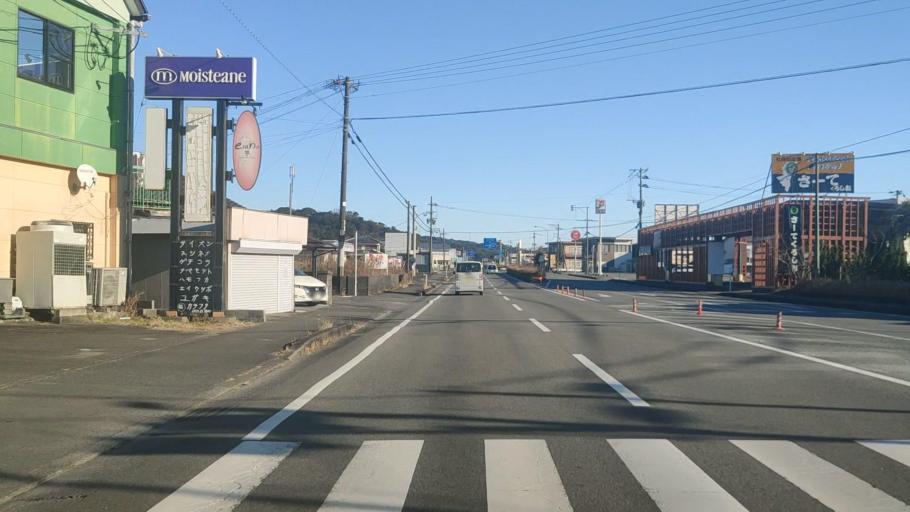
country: JP
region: Miyazaki
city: Nobeoka
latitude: 32.4757
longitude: 131.6536
